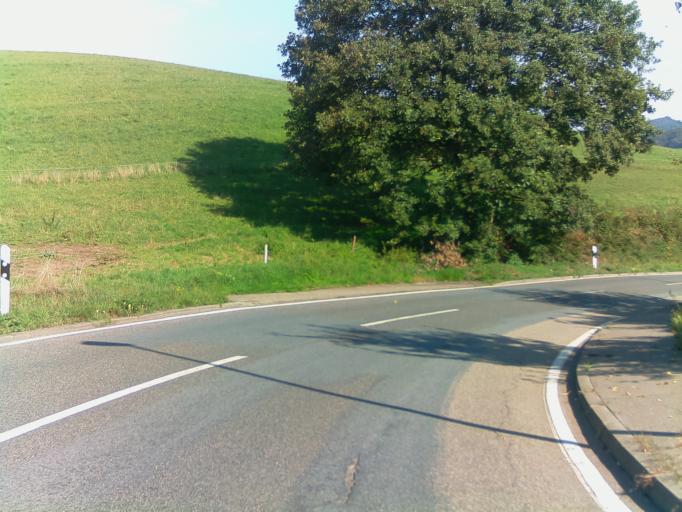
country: DE
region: Hesse
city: Unter-Abtsteinach
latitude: 49.5141
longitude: 8.7447
